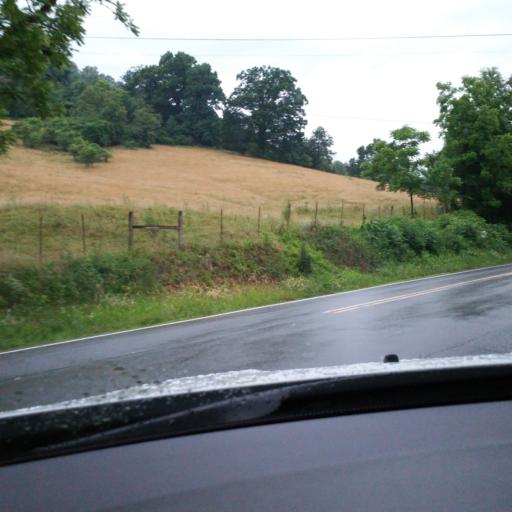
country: US
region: North Carolina
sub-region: Yancey County
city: Burnsville
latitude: 35.9055
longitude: -82.2939
